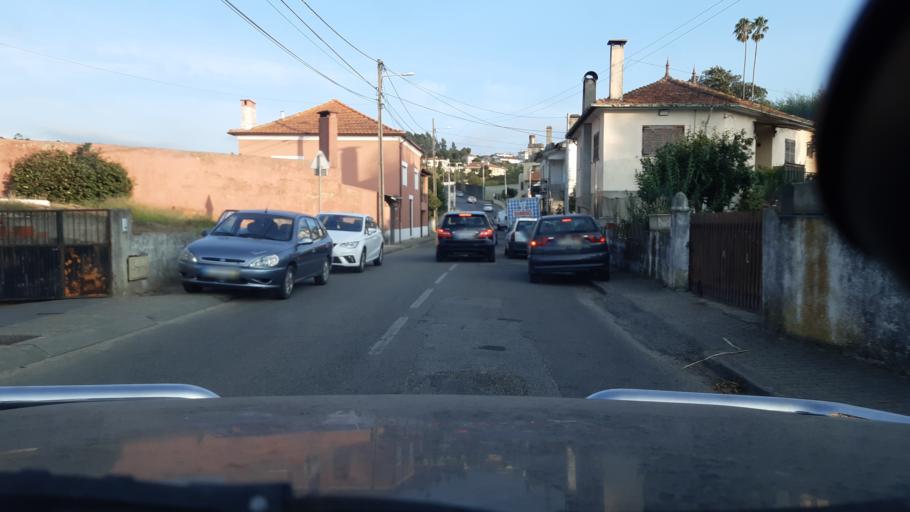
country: PT
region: Aveiro
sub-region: Agueda
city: Agueda
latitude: 40.5604
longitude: -8.4373
